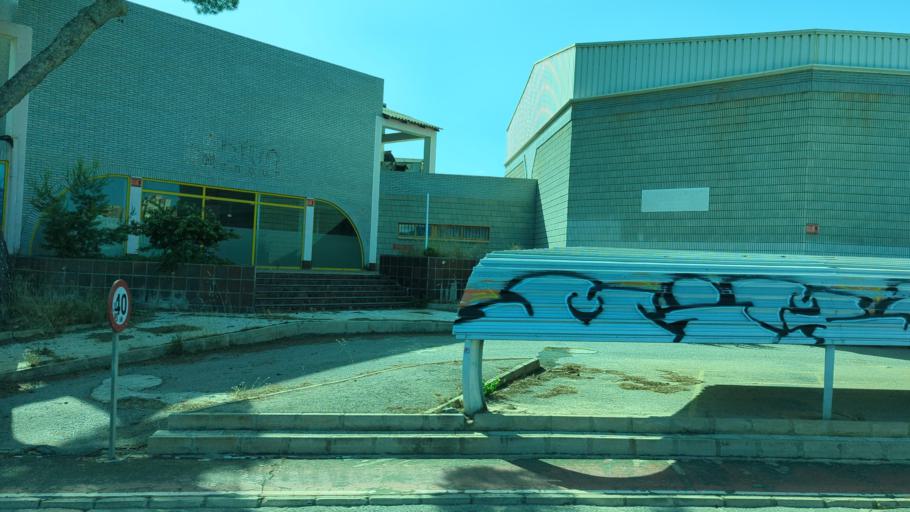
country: ES
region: Valencia
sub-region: Provincia de Alicante
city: Pilar de la Horadada
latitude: 37.8940
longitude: -0.7591
